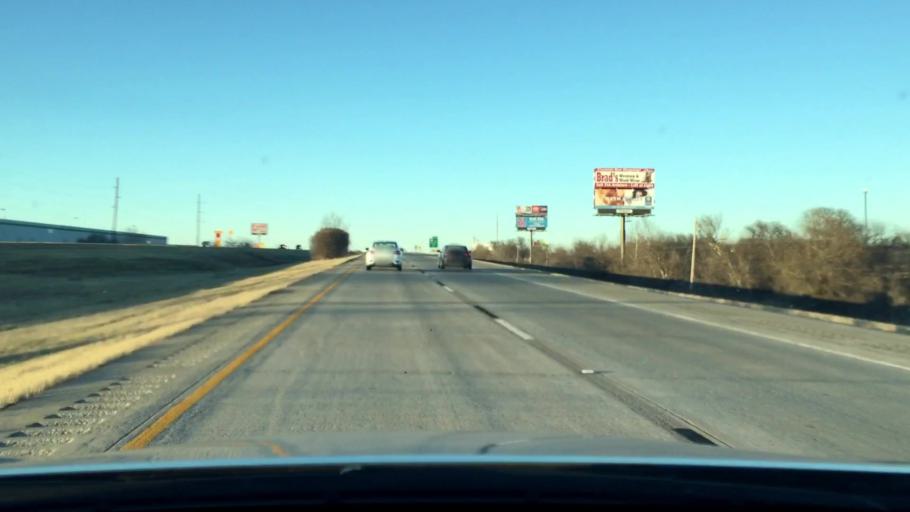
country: US
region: Oklahoma
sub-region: Love County
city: Marietta
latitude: 33.9322
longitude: -97.1347
